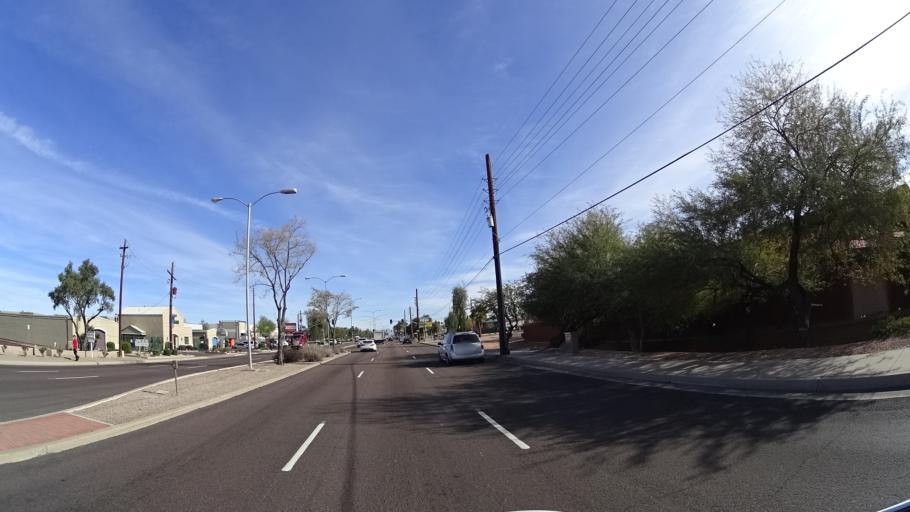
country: US
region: Arizona
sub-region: Maricopa County
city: Tempe
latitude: 33.4074
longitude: -111.8846
